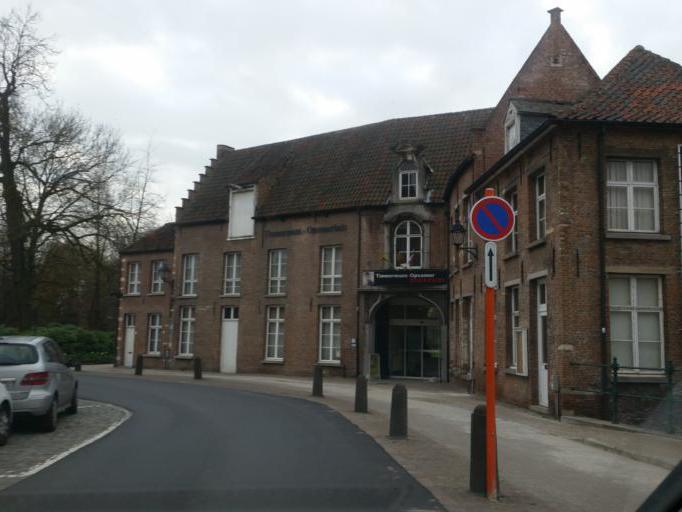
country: BE
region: Flanders
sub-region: Provincie Antwerpen
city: Lier
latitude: 51.1288
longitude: 4.5708
